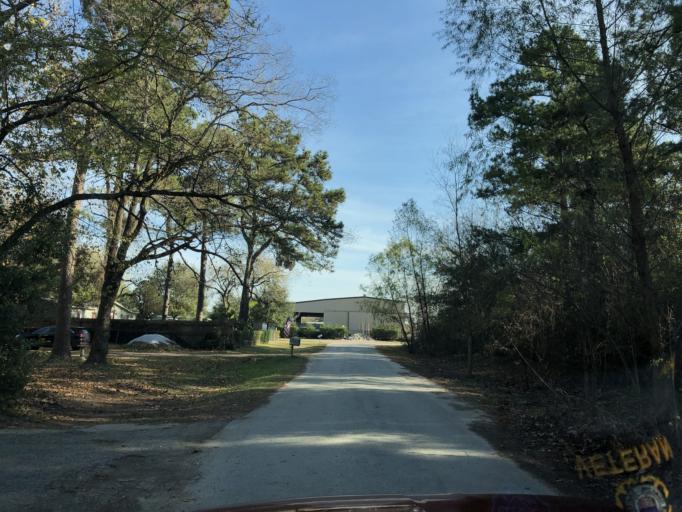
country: US
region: Texas
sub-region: Harris County
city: Tomball
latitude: 30.0438
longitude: -95.5462
